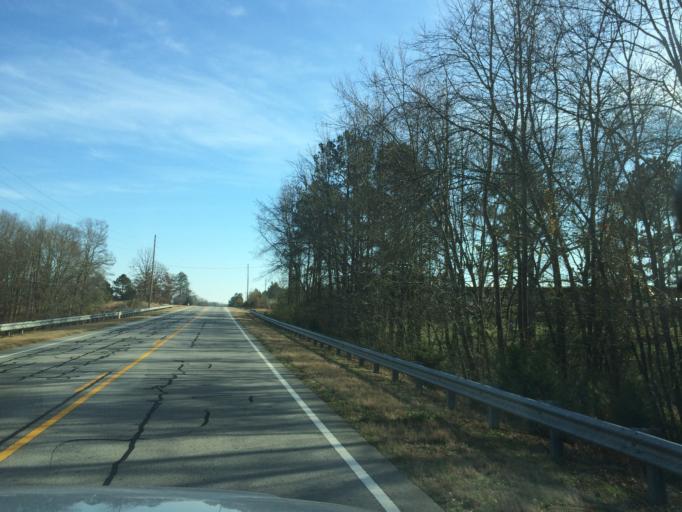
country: US
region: Georgia
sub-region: Franklin County
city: Gumlog
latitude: 34.4598
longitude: -83.0544
